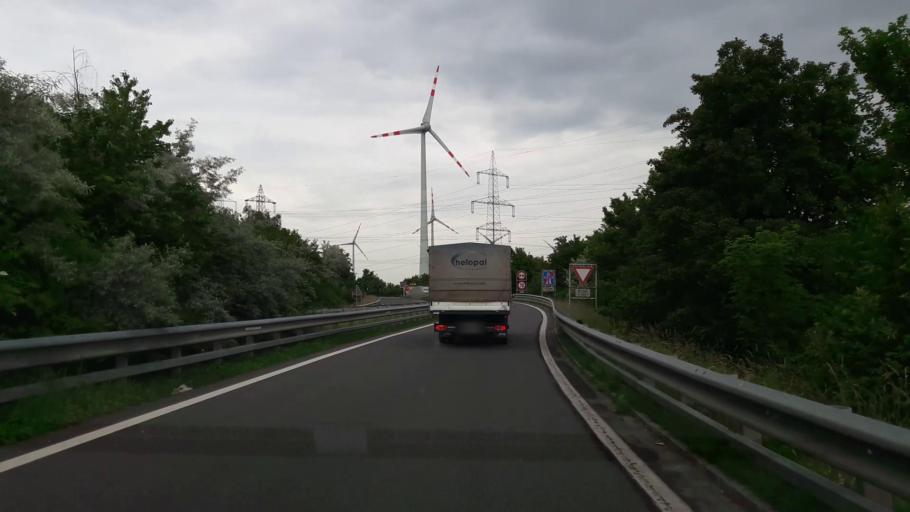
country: AT
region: Burgenland
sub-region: Politischer Bezirk Neusiedl am See
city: Bruckneudorf
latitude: 48.0357
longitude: 16.8163
